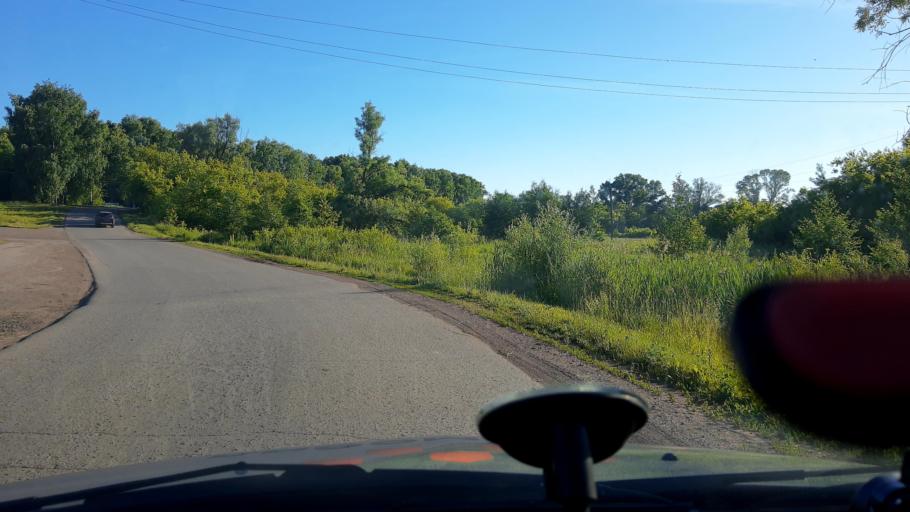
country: RU
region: Bashkortostan
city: Chishmy
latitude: 54.6002
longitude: 55.3764
